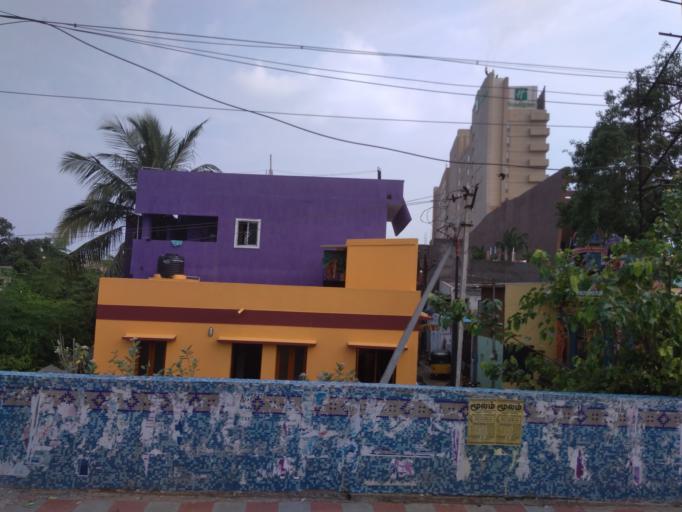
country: IN
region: Tamil Nadu
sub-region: Kancheepuram
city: Perungudi
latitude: 12.9818
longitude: 80.2533
